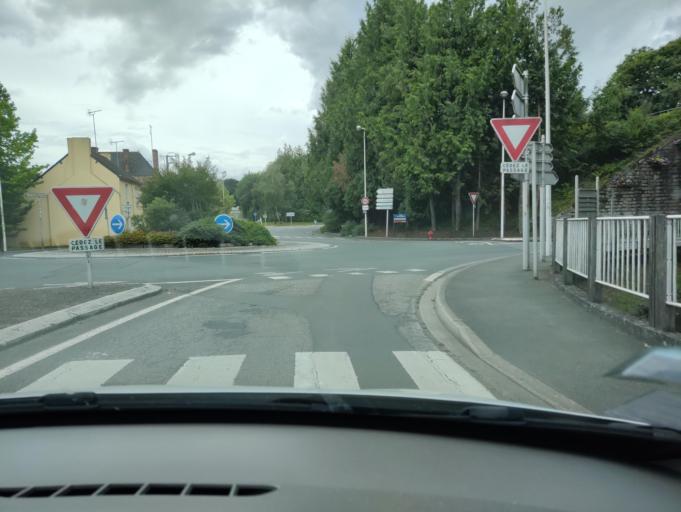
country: FR
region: Pays de la Loire
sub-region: Departement de la Loire-Atlantique
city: Chateaubriant
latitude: 47.7104
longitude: -1.3729
